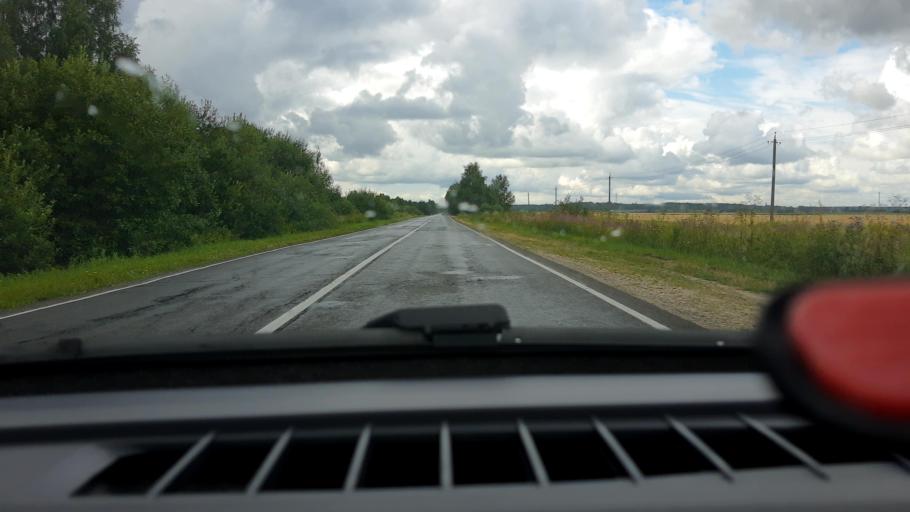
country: RU
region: Nizjnij Novgorod
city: Neklyudovo
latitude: 56.5242
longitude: 43.8665
